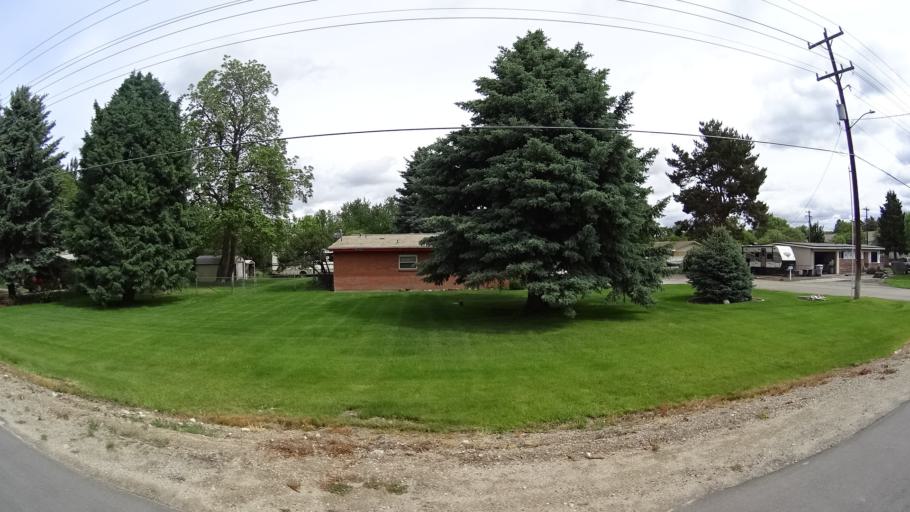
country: US
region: Idaho
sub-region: Ada County
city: Eagle
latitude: 43.6955
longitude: -116.3649
